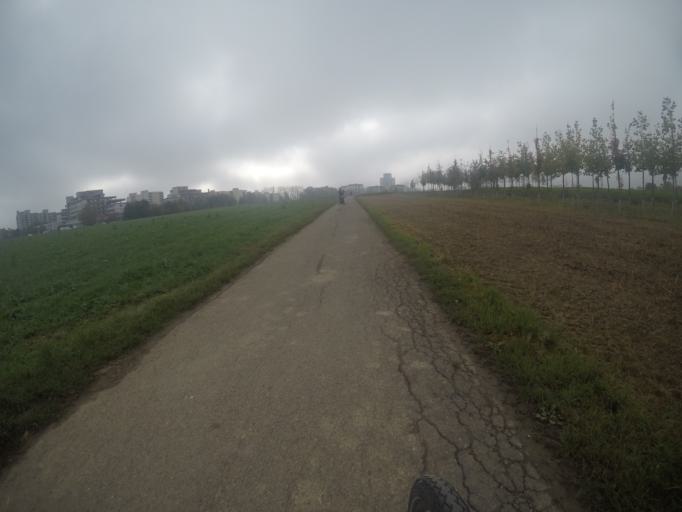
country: DE
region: Baden-Wuerttemberg
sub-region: Regierungsbezirk Stuttgart
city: Leinfelden-Echterdingen
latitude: 48.7343
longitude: 9.1336
